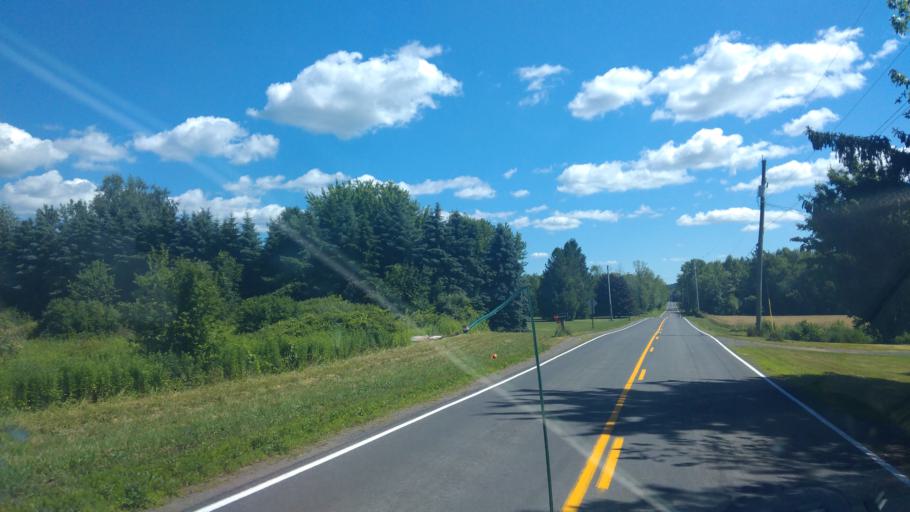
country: US
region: New York
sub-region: Wayne County
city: Sodus
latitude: 43.1884
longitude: -77.0504
